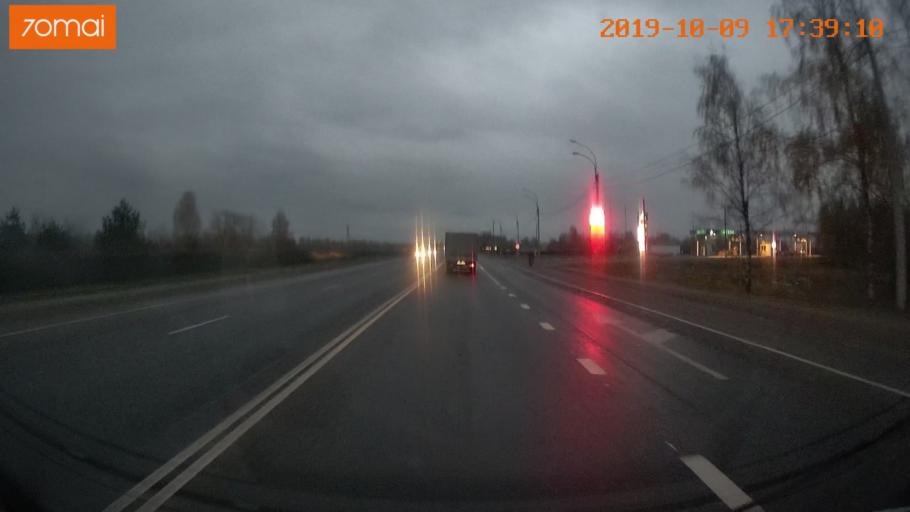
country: RU
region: Ivanovo
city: Bogorodskoye
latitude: 57.0633
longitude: 40.9549
